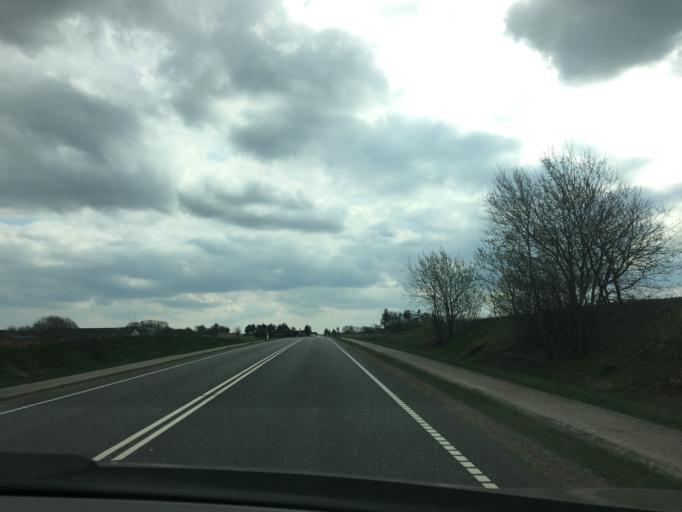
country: DK
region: Central Jutland
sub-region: Horsens Kommune
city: Braedstrup
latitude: 55.9944
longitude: 9.6044
